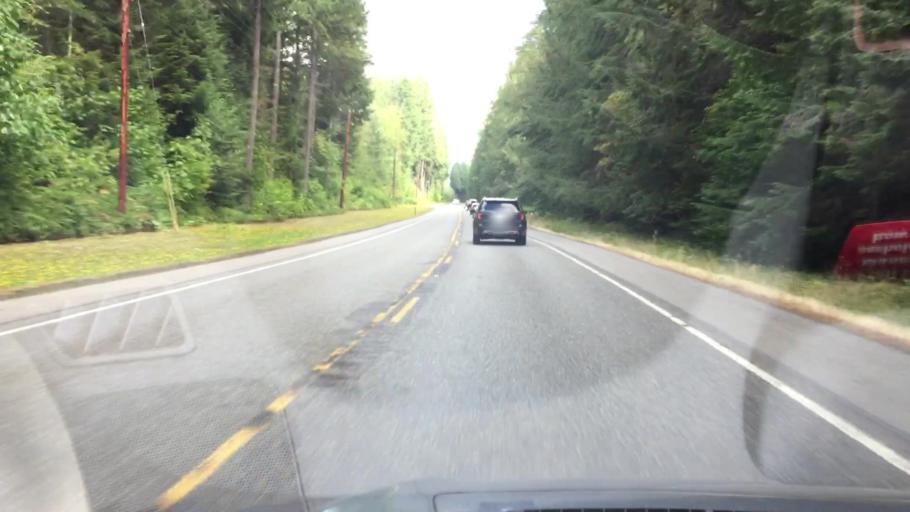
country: US
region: Washington
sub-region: Pierce County
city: Eatonville
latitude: 46.7536
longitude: -122.1074
